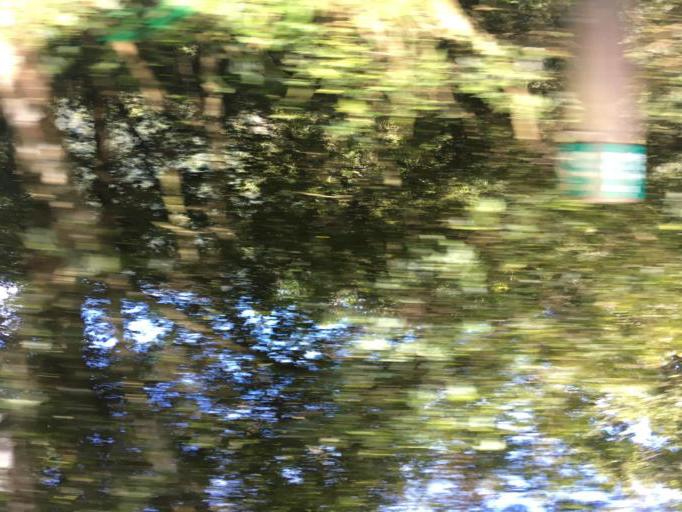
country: TW
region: Taiwan
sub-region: Yilan
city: Yilan
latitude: 24.5457
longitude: 121.5130
